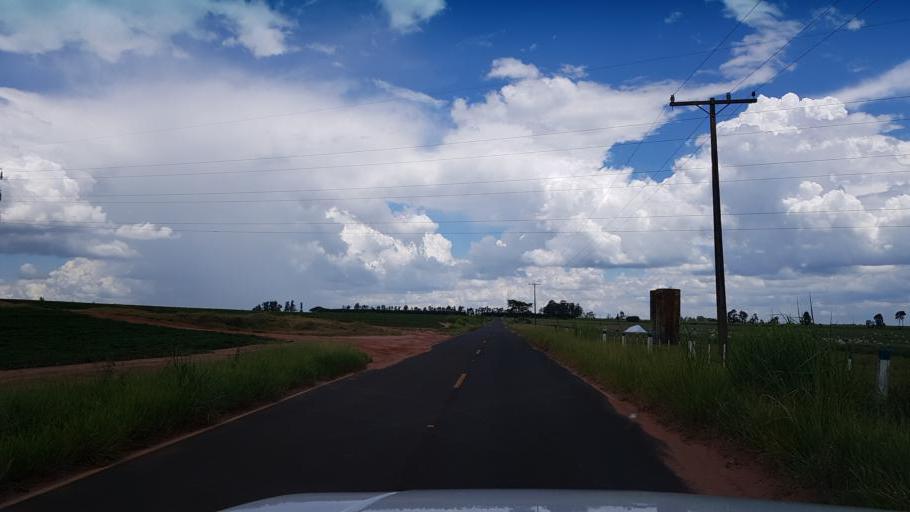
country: BR
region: Sao Paulo
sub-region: Paraguacu Paulista
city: Paraguacu Paulista
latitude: -22.3579
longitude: -50.6263
